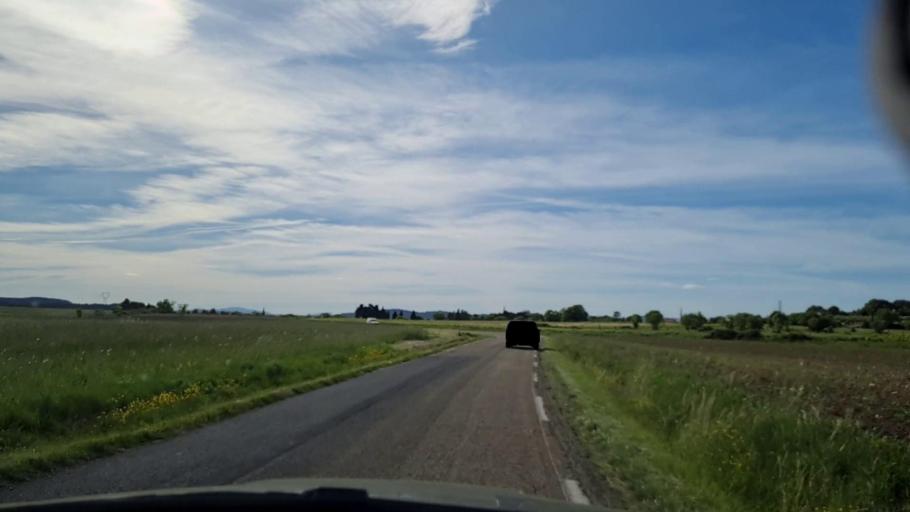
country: FR
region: Languedoc-Roussillon
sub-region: Departement du Gard
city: Villevieille
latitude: 43.8276
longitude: 4.1009
